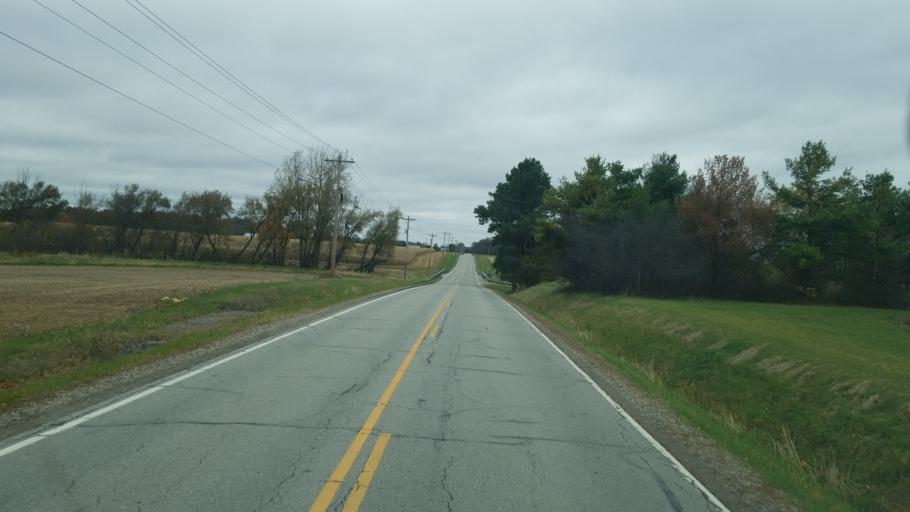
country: US
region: Ohio
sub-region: Huron County
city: Willard
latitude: 40.9845
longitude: -82.8533
